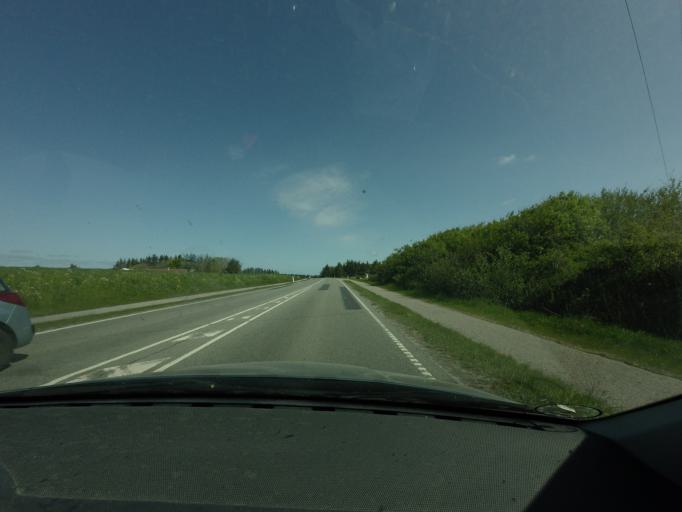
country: DK
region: North Denmark
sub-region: Jammerbugt Kommune
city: Pandrup
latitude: 57.3182
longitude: 9.7094
